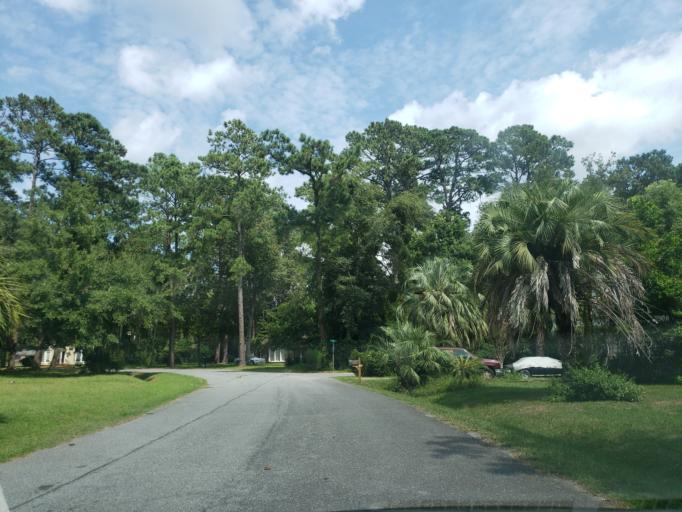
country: US
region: Georgia
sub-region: Chatham County
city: Isle of Hope
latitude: 31.9877
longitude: -81.0509
